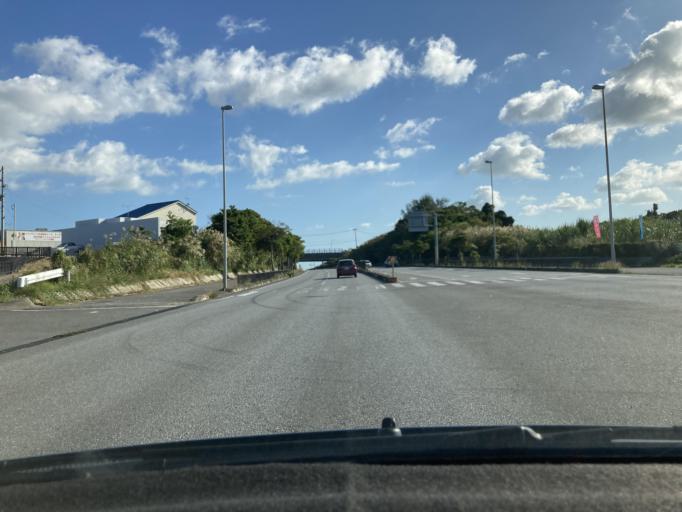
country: JP
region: Okinawa
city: Ishikawa
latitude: 26.4180
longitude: 127.8158
